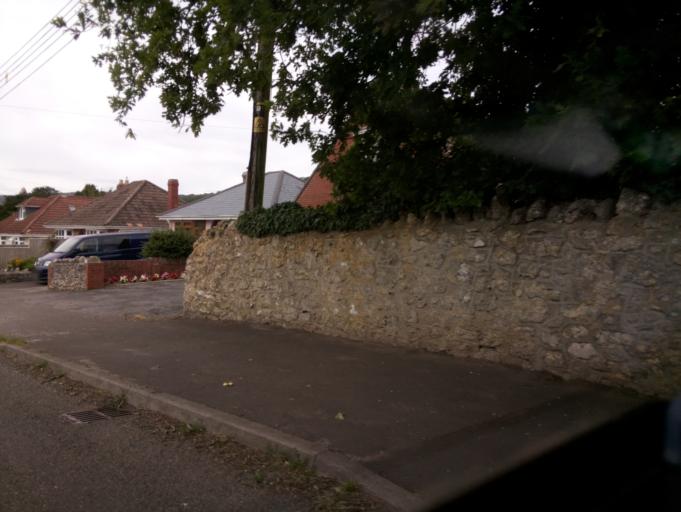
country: GB
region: England
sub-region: Somerset
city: Wells
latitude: 51.2248
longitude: -2.6976
